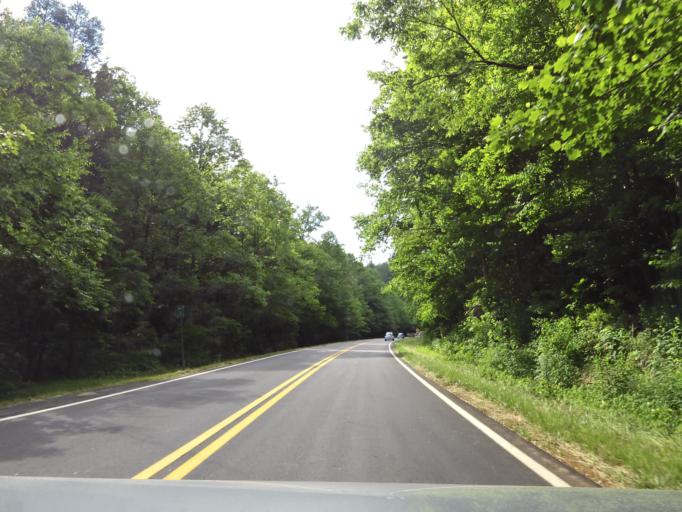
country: US
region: Georgia
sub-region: Towns County
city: Hiawassee
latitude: 34.8351
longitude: -83.7659
